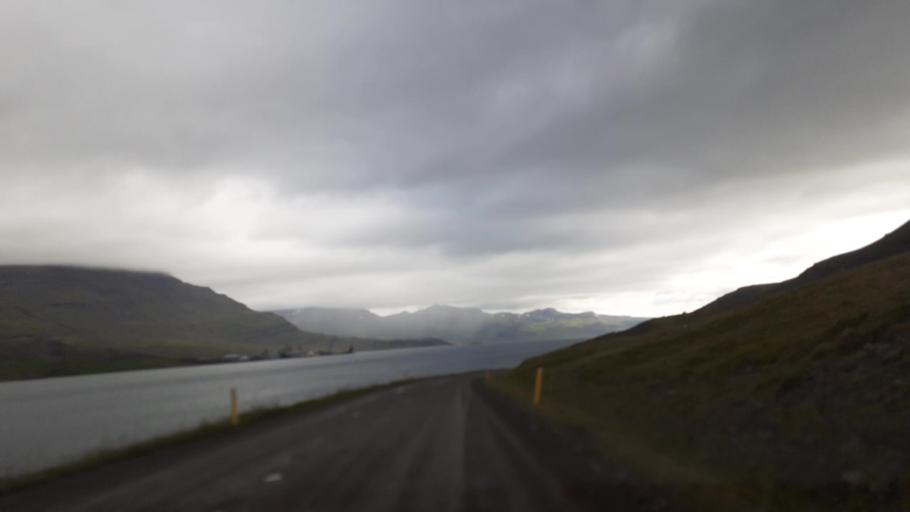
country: IS
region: East
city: Reydarfjoerdur
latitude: 65.0126
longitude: -14.1756
